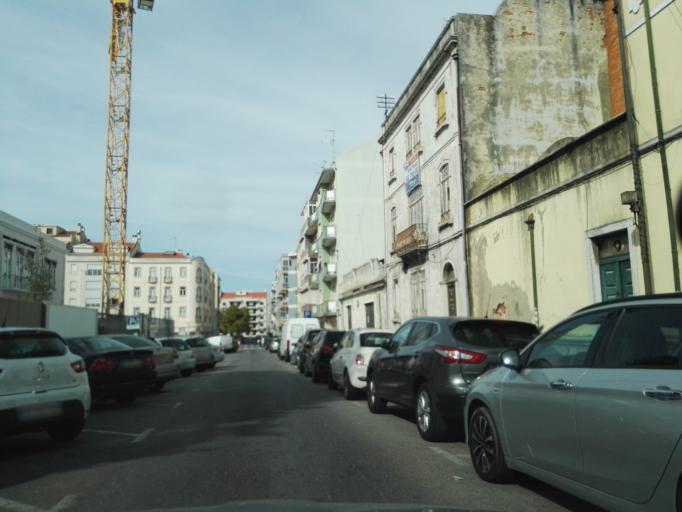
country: PT
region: Lisbon
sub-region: Lisbon
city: Lisbon
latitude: 38.7184
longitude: -9.1664
